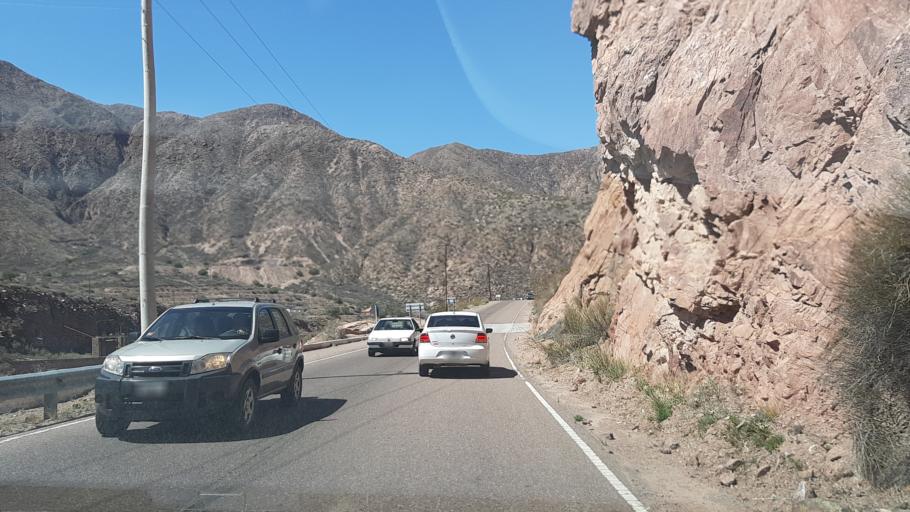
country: AR
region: Mendoza
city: Lujan de Cuyo
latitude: -33.0055
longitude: -69.1251
